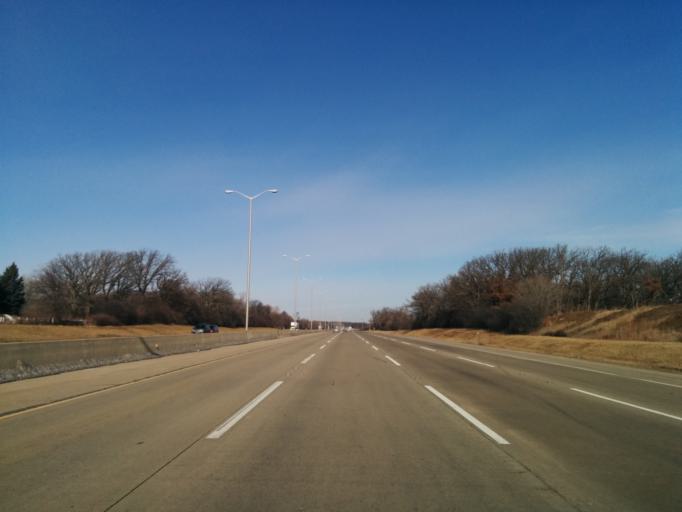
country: US
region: Illinois
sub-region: Lake County
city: Wadsworth
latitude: 42.4023
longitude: -87.9485
